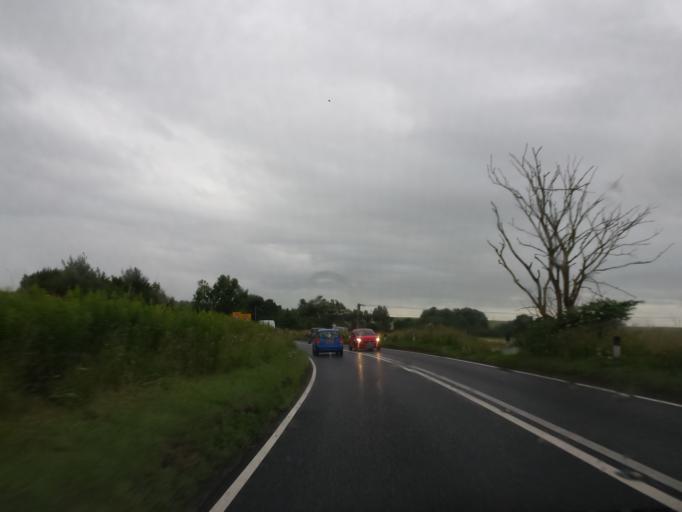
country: GB
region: Scotland
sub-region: Fife
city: Newport-On-Tay
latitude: 56.4134
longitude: -2.9166
